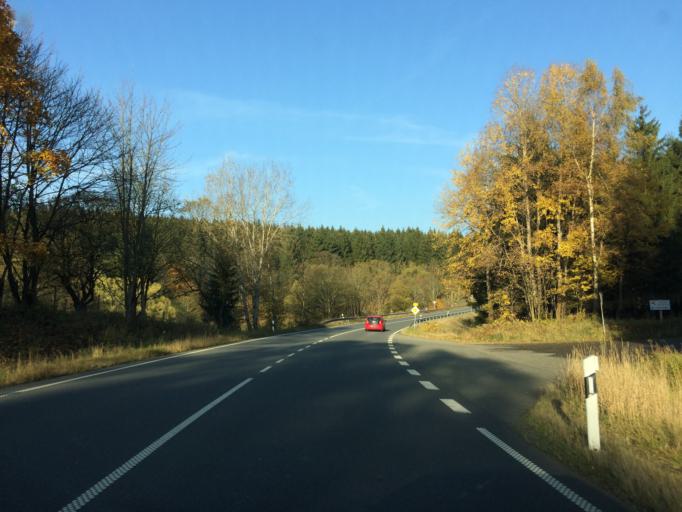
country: DE
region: Lower Saxony
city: Braunlage
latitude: 51.7124
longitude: 10.5923
